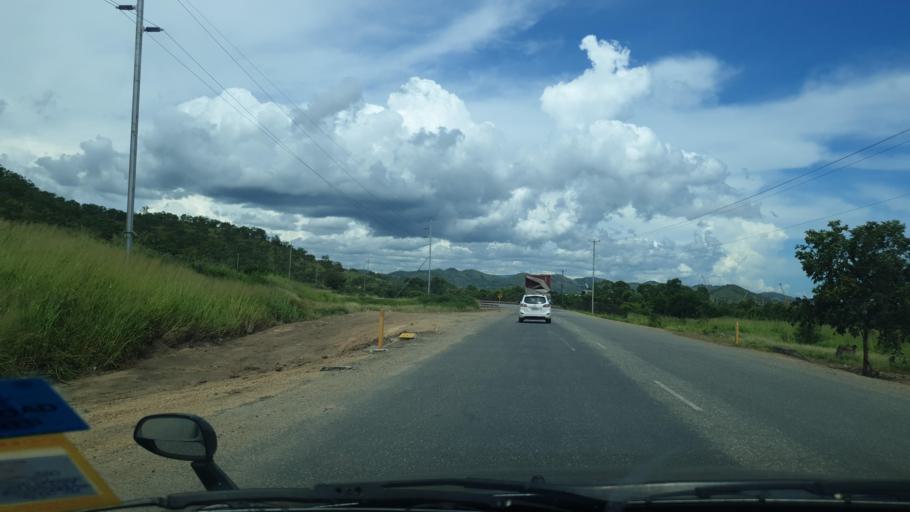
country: PG
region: National Capital
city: Port Moresby
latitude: -9.4197
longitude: 147.0911
